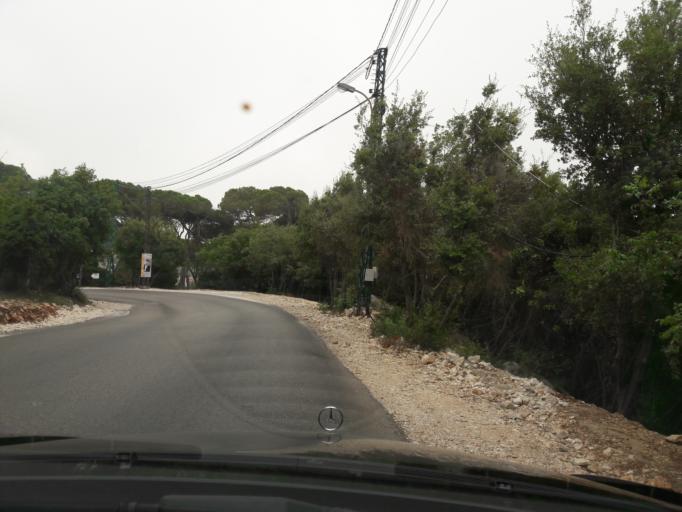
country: LB
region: Mont-Liban
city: Djounie
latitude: 33.9884
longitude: 35.6774
